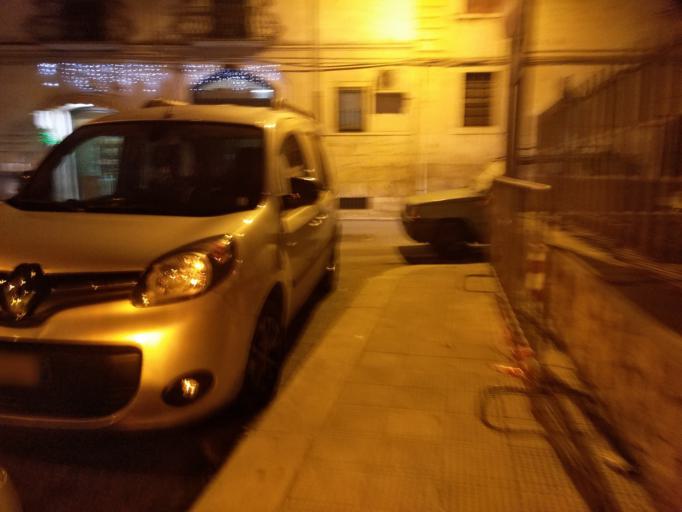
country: IT
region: Apulia
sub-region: Provincia di Bari
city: Modugno
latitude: 41.0807
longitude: 16.7830
